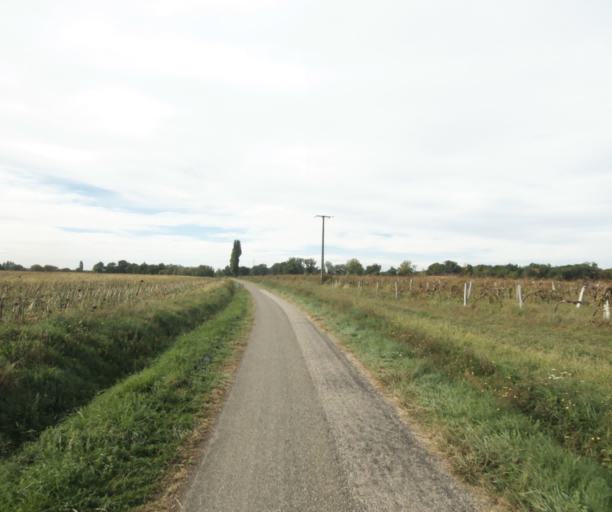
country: FR
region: Midi-Pyrenees
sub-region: Departement du Gers
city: Le Houga
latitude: 43.8767
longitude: -0.1696
